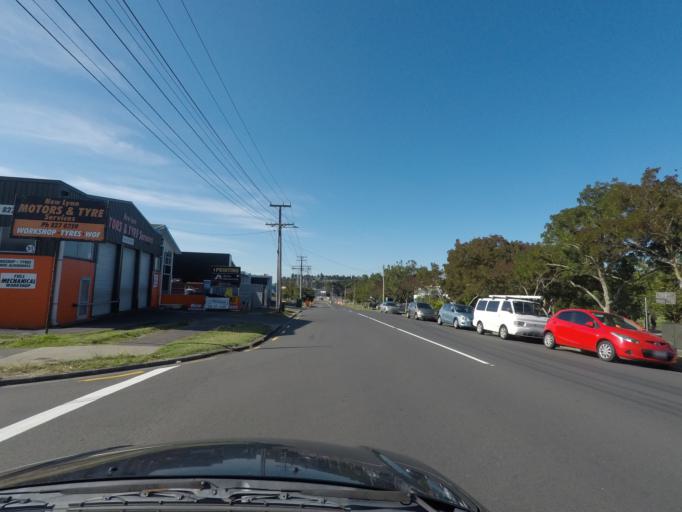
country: NZ
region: Auckland
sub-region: Auckland
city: Waitakere
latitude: -36.9094
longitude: 174.6897
